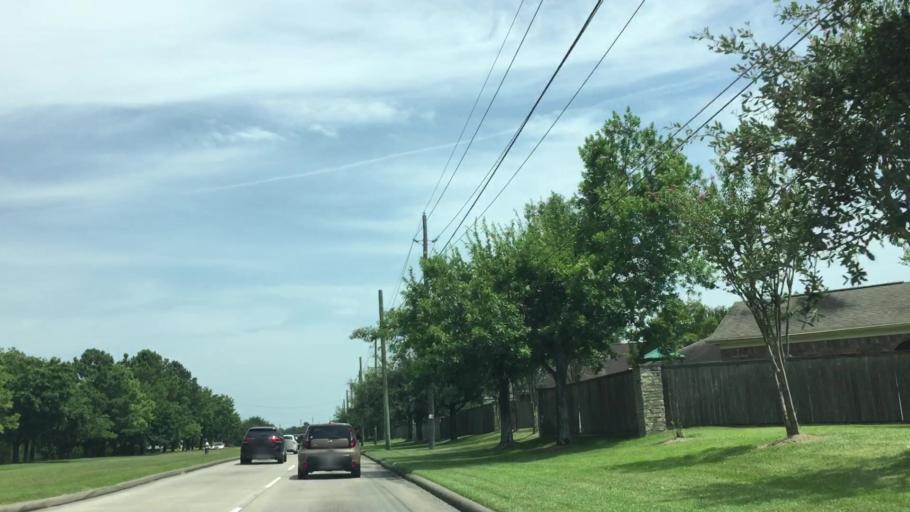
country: US
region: Texas
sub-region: Harris County
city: Jersey Village
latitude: 29.9079
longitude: -95.5630
